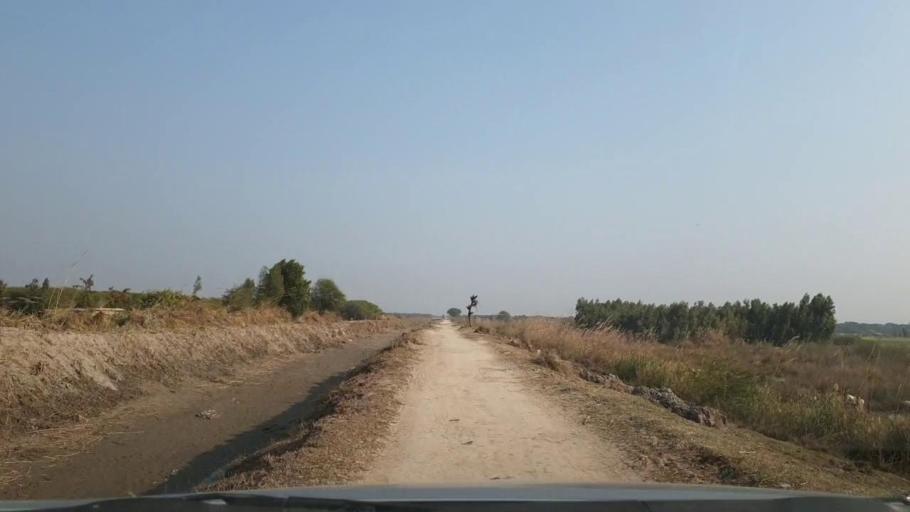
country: PK
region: Sindh
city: Tando Adam
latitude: 25.6468
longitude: 68.5987
